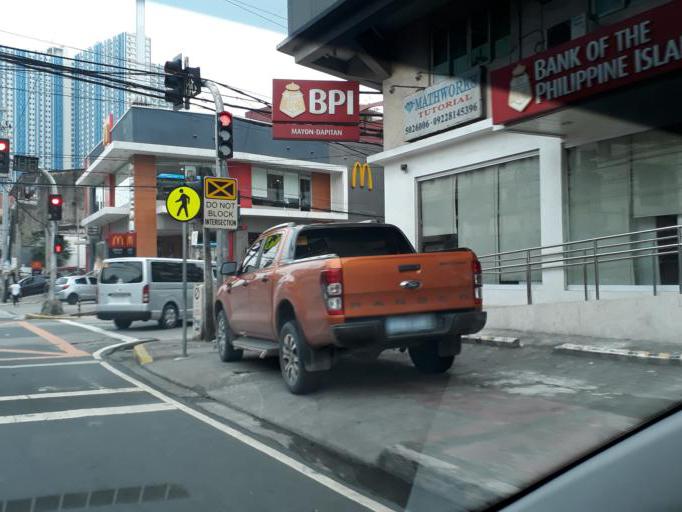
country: PH
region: Metro Manila
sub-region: City of Manila
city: Manila
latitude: 14.6222
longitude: 120.9996
